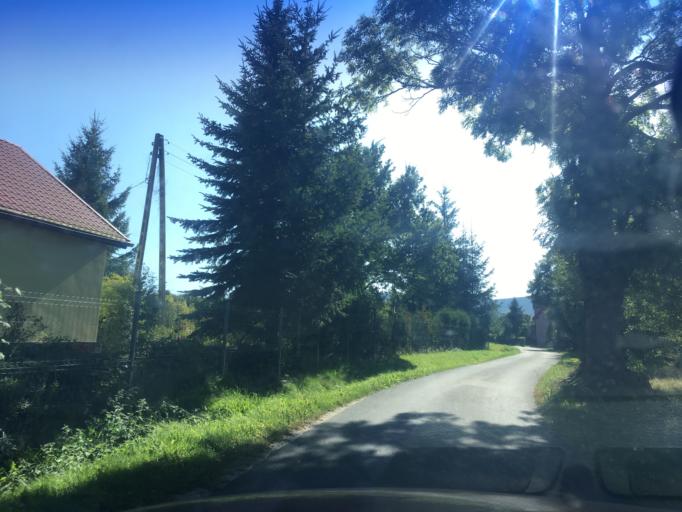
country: PL
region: Lower Silesian Voivodeship
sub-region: Powiat lubanski
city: Swieradow-Zdroj
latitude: 50.9526
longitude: 15.3199
